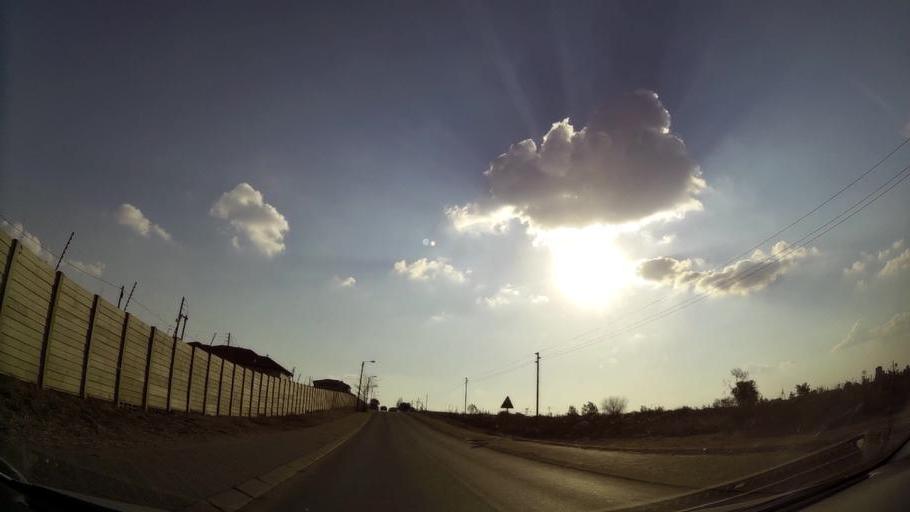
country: ZA
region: Gauteng
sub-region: Ekurhuleni Metropolitan Municipality
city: Tembisa
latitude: -25.9516
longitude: 28.2062
